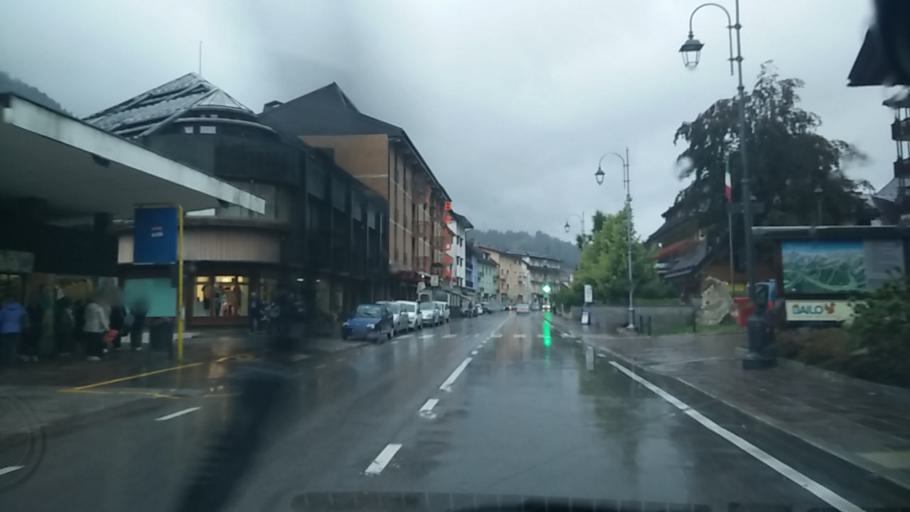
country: IT
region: Friuli Venezia Giulia
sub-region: Provincia di Udine
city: Tarvisio
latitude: 46.5053
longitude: 13.5773
